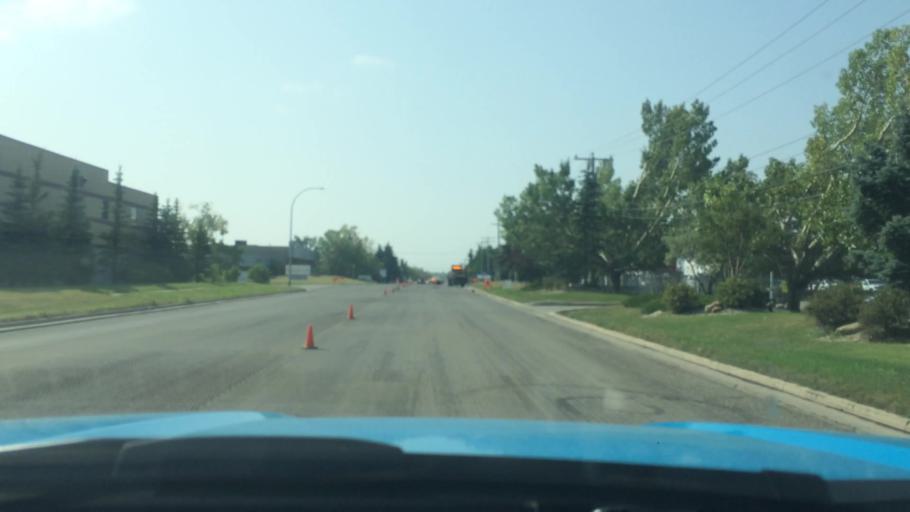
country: CA
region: Alberta
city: Calgary
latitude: 51.0908
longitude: -114.0116
